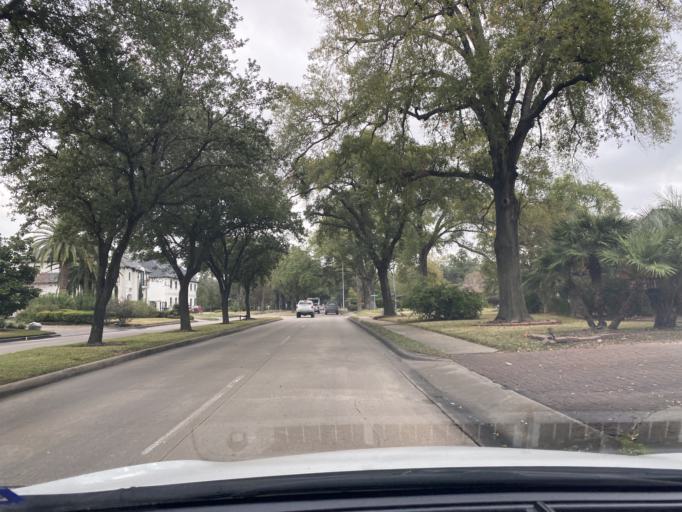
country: US
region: Texas
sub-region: Harris County
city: Hunters Creek Village
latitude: 29.7529
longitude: -95.4772
